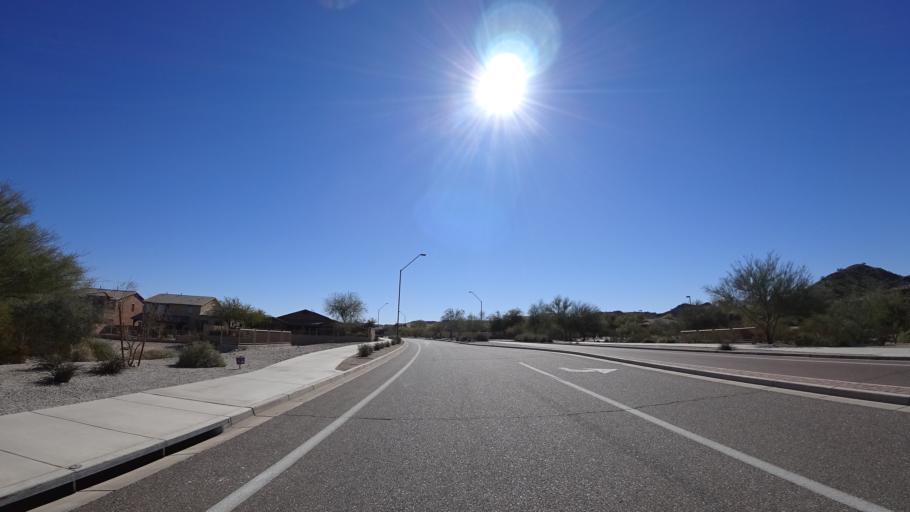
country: US
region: Arizona
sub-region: Maricopa County
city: Goodyear
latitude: 33.3264
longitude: -112.4478
